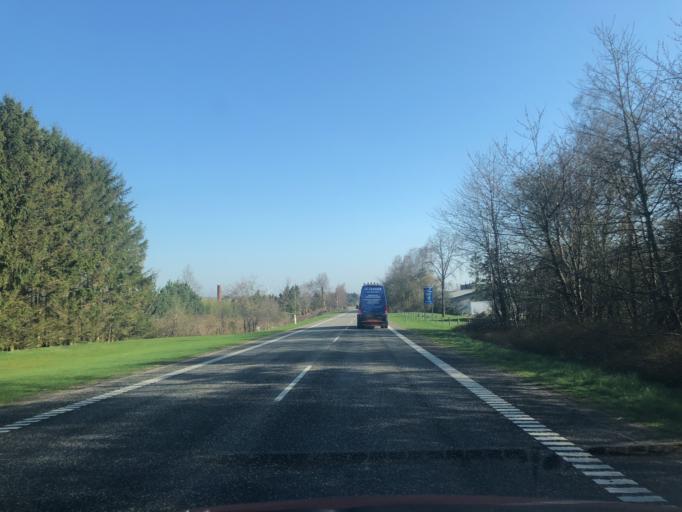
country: DK
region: Zealand
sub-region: Faxe Kommune
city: Ronnede
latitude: 55.2620
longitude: 12.0229
